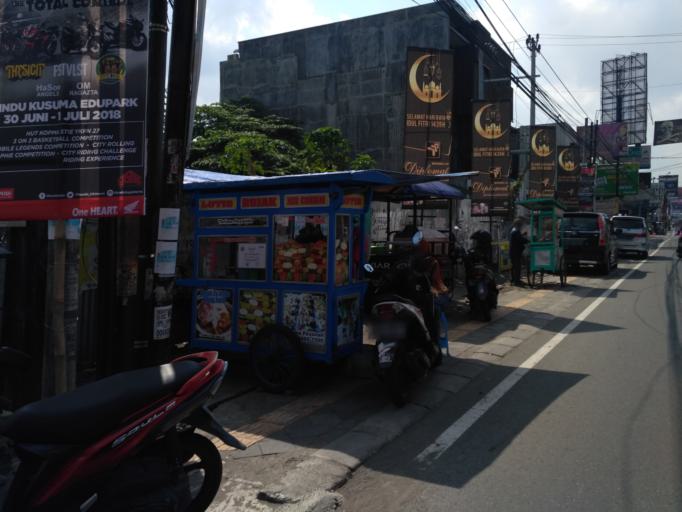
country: ID
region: Daerah Istimewa Yogyakarta
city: Depok
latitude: -7.7718
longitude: 110.4093
